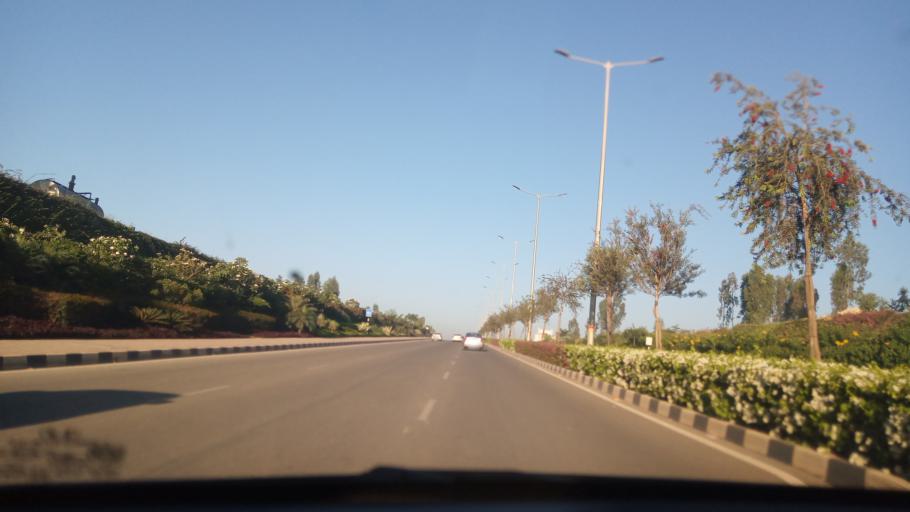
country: IN
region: Karnataka
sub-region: Bangalore Rural
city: Devanhalli
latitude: 13.1947
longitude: 77.6914
